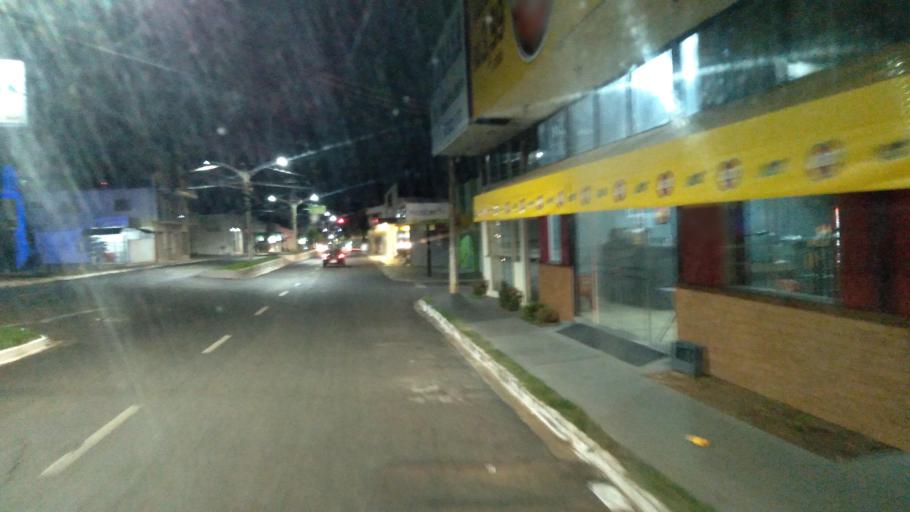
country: BR
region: Goias
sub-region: Mineiros
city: Mineiros
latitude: -17.5649
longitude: -52.5582
